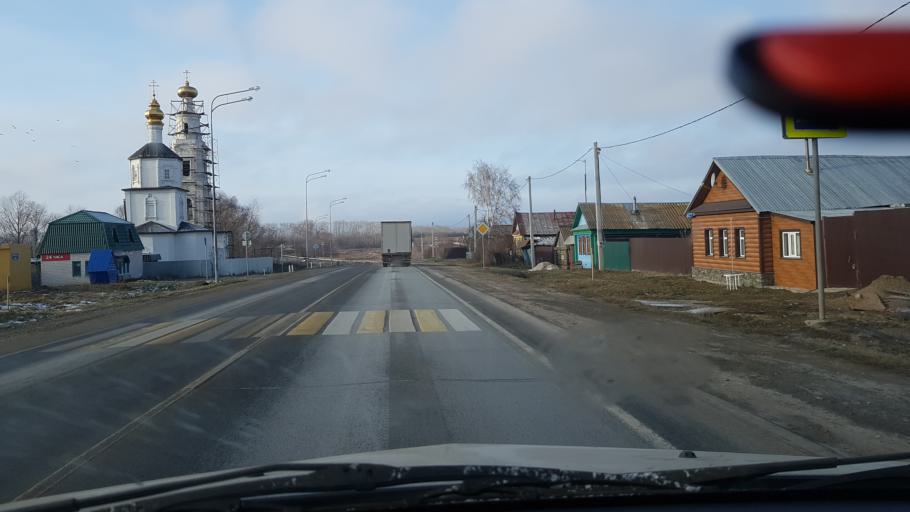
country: RU
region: Tatarstan
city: Laishevo
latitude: 55.3920
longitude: 49.8023
